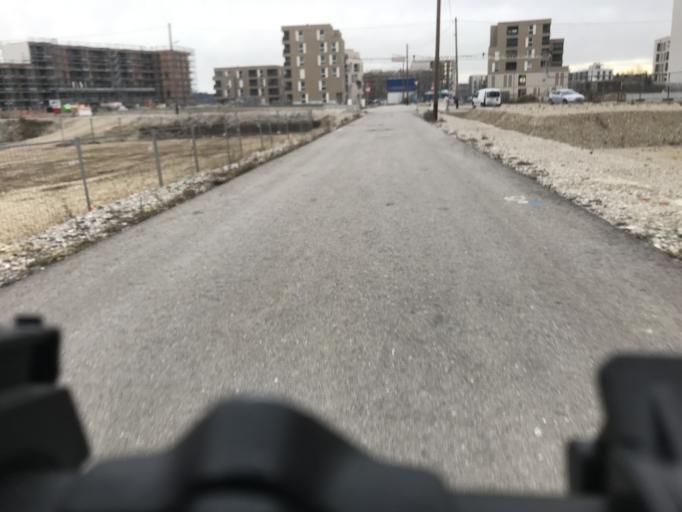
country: DE
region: Bavaria
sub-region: Upper Bavaria
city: Germering
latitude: 48.1482
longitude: 11.4070
